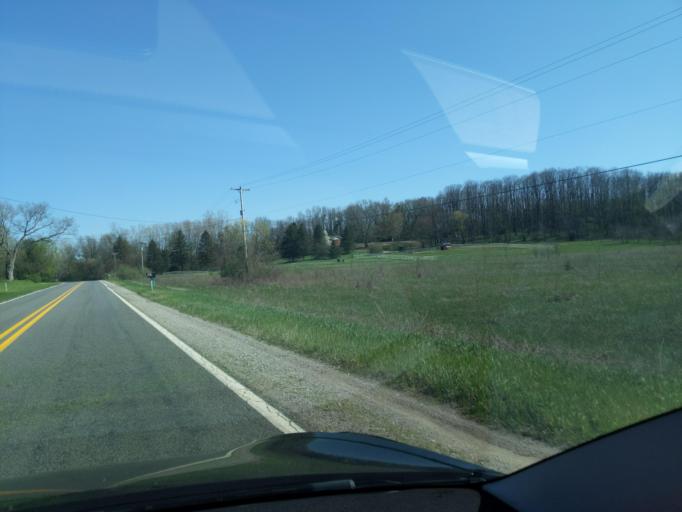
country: US
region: Michigan
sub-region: Ingham County
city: Stockbridge
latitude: 42.4344
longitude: -84.0911
